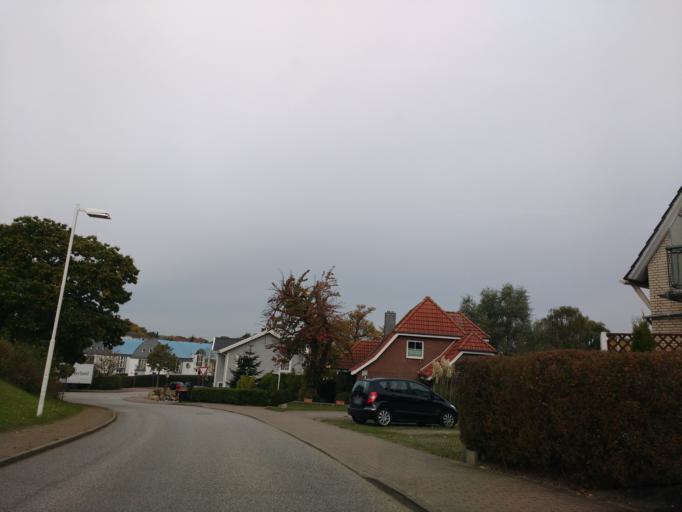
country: DE
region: Schleswig-Holstein
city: Gromitz
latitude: 54.1531
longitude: 10.9606
